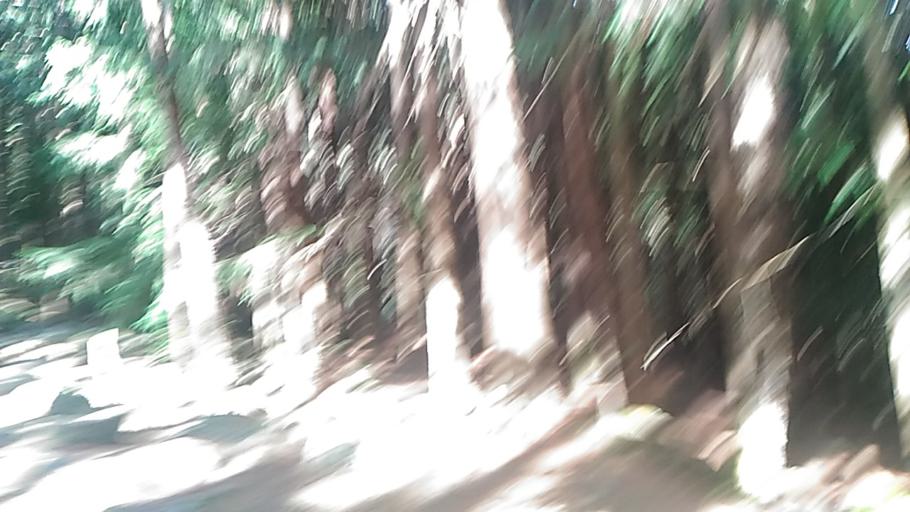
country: TW
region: Taiwan
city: Daxi
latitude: 24.3998
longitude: 121.3078
